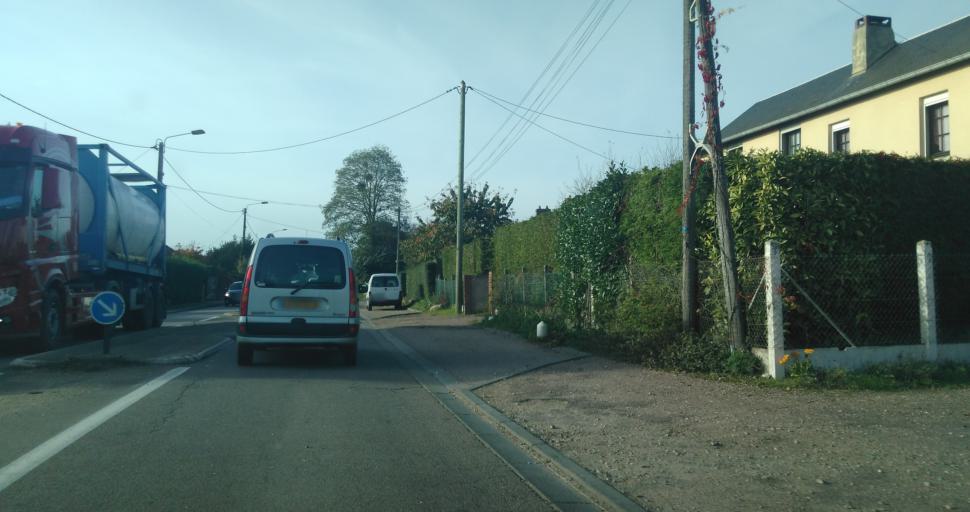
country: FR
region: Haute-Normandie
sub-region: Departement de l'Eure
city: Saint-Ouen-de-Thouberville
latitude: 49.3566
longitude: 0.8843
